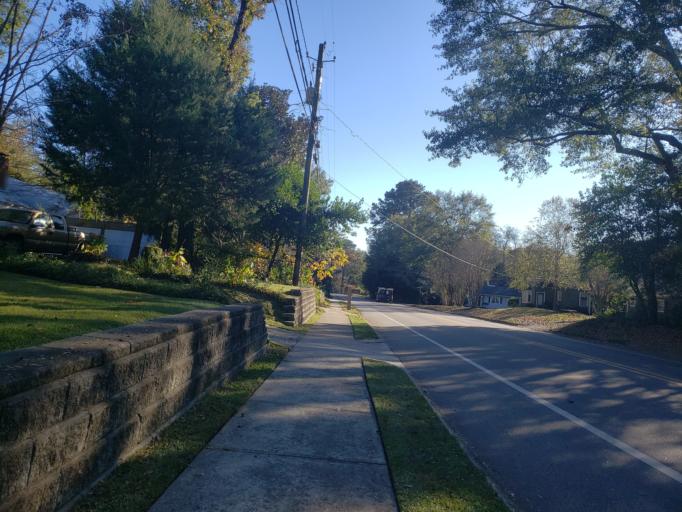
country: US
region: Alabama
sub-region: Lee County
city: Auburn
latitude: 32.5933
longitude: -85.4800
